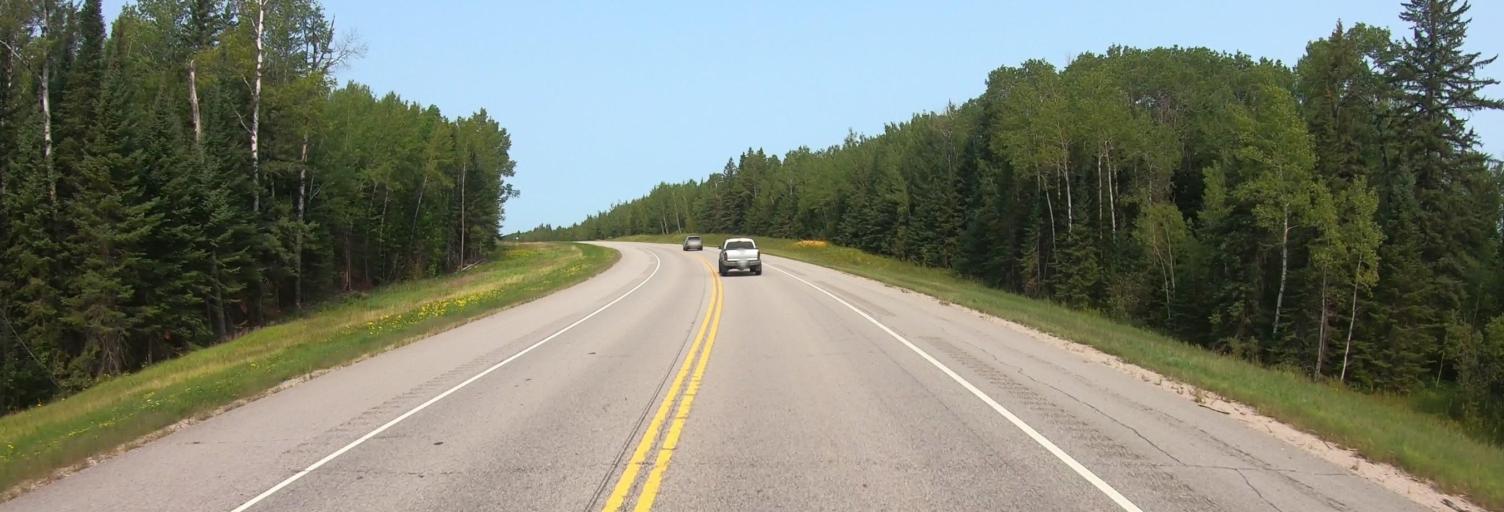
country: CA
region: Ontario
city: Fort Frances
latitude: 48.3649
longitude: -92.9638
